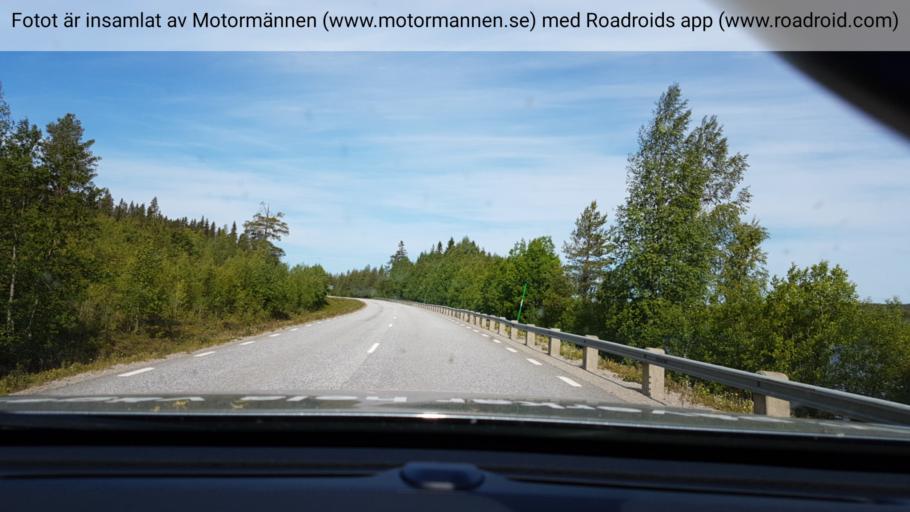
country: SE
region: Vaesterbotten
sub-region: Dorotea Kommun
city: Dorotea
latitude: 64.2371
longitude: 16.7934
